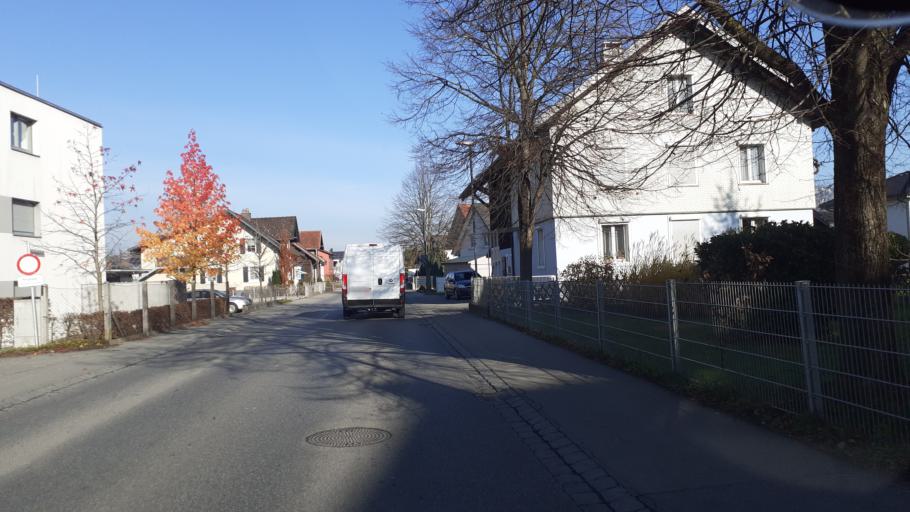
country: AT
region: Vorarlberg
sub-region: Politischer Bezirk Feldkirch
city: Nofels
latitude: 47.2603
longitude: 9.5912
